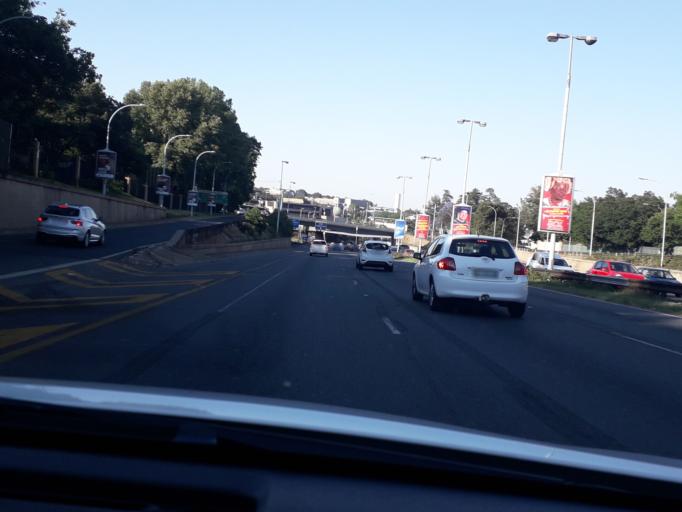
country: ZA
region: Gauteng
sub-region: City of Johannesburg Metropolitan Municipality
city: Johannesburg
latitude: -26.1810
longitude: 28.0347
